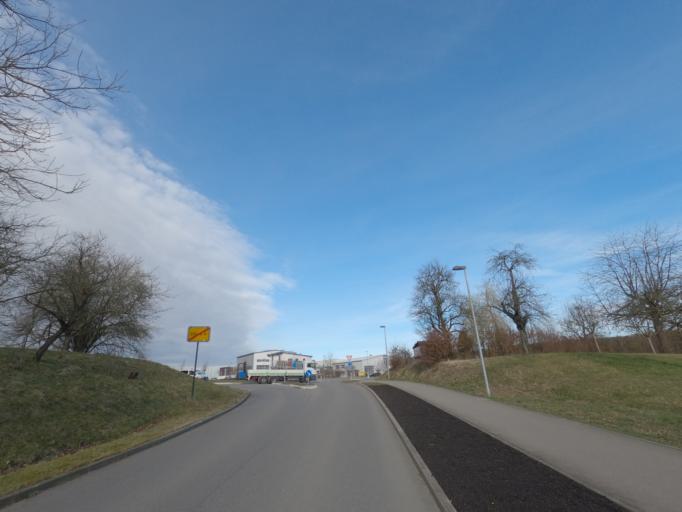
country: DE
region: Baden-Wuerttemberg
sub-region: Regierungsbezirk Stuttgart
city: Zell unter Aichelberg
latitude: 48.6483
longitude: 9.5656
